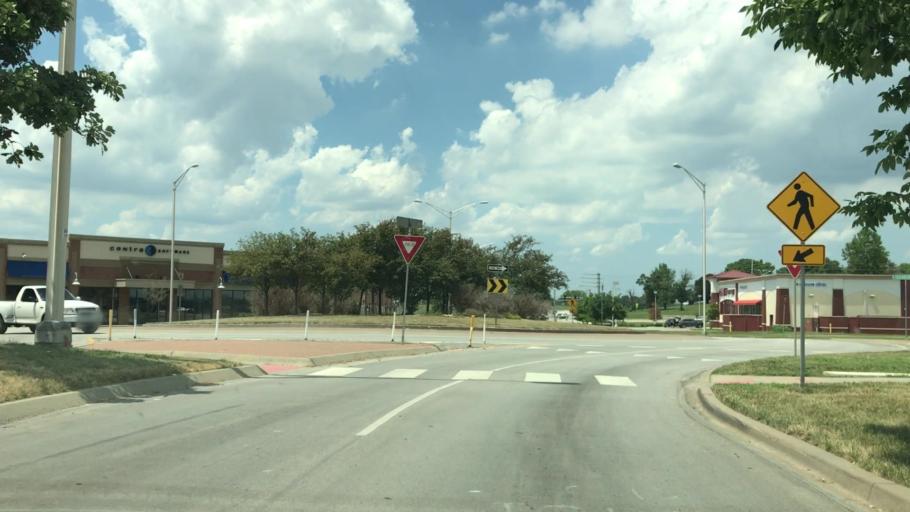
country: US
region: Missouri
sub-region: Jackson County
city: Lees Summit
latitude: 38.9113
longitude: -94.4492
